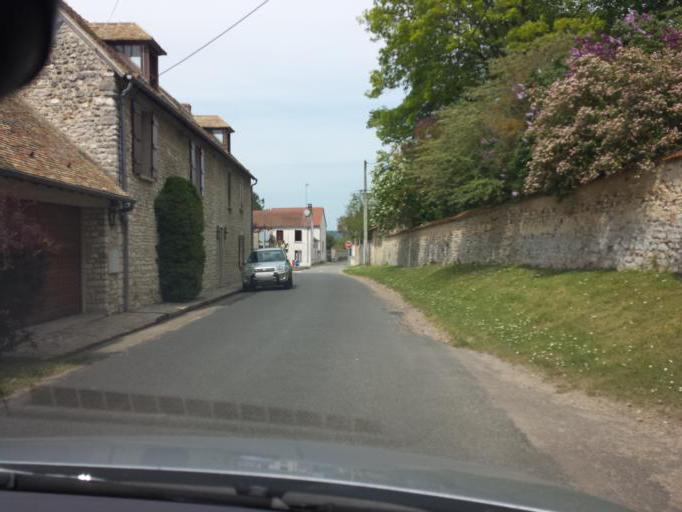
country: FR
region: Centre
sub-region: Departement d'Eure-et-Loir
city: Oulins
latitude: 48.8642
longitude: 1.4706
